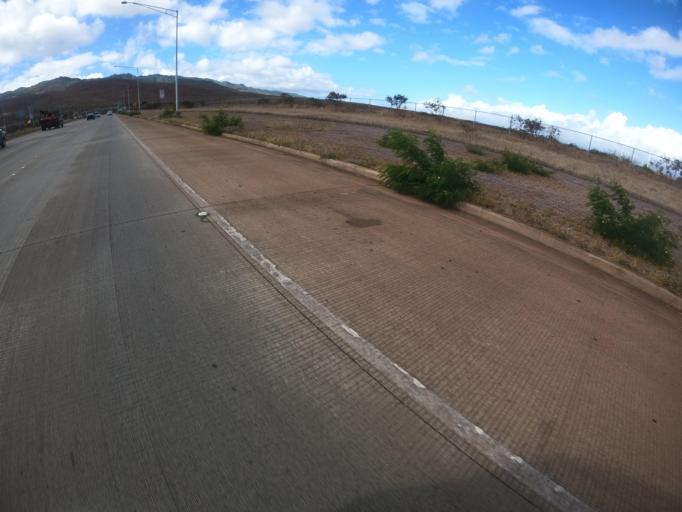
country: US
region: Hawaii
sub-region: Honolulu County
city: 'Ewa Villages
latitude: 21.3630
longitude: -158.0562
